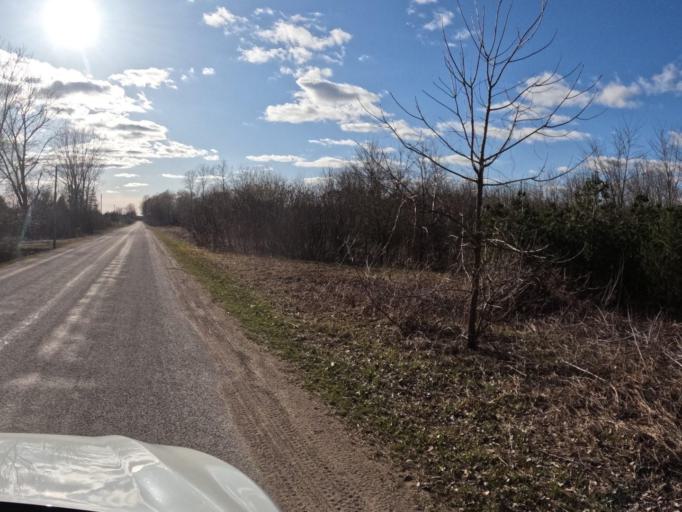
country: CA
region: Ontario
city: Norfolk County
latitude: 42.8154
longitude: -80.5580
